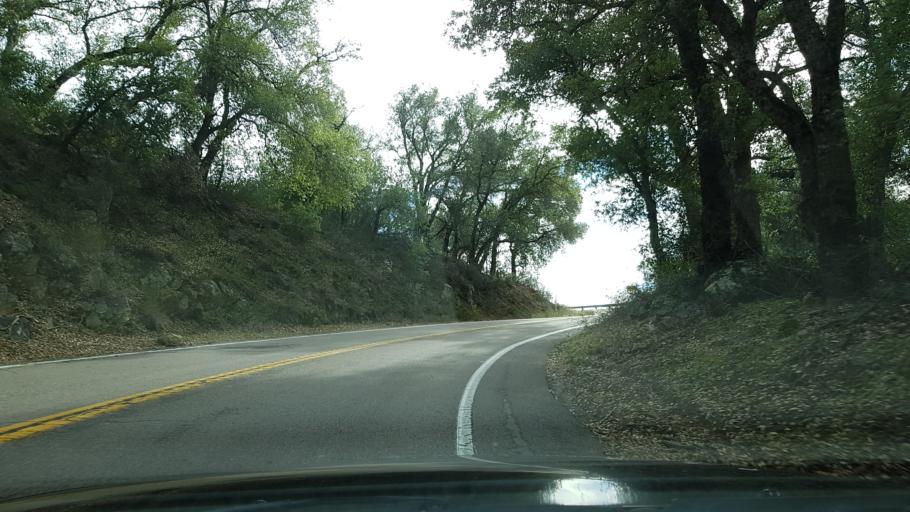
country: US
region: California
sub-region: Riverside County
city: Aguanga
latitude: 33.3038
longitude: -116.8862
